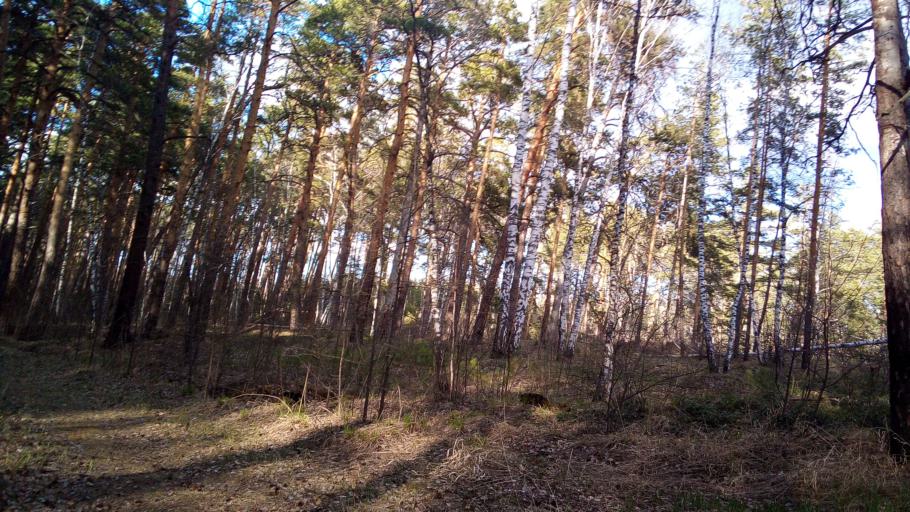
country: RU
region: Chelyabinsk
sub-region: Gorod Chelyabinsk
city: Chelyabinsk
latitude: 55.1636
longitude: 61.3211
